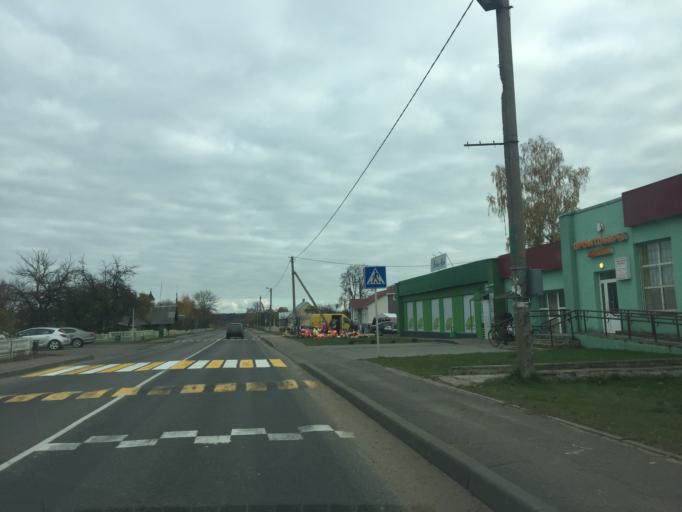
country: BY
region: Minsk
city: Svir
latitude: 54.8127
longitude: 26.1580
